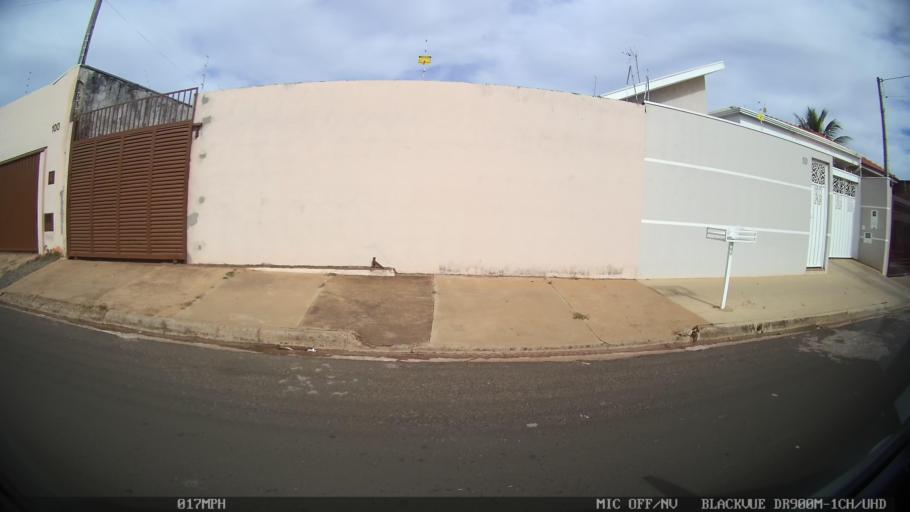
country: BR
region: Sao Paulo
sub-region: Catanduva
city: Catanduva
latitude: -21.1578
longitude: -48.9736
